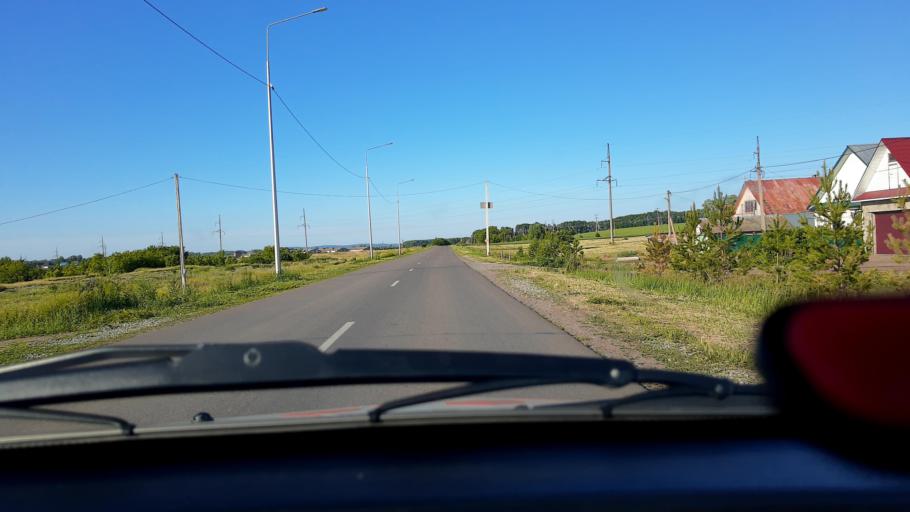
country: RU
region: Bashkortostan
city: Kabakovo
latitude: 54.5040
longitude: 55.9248
